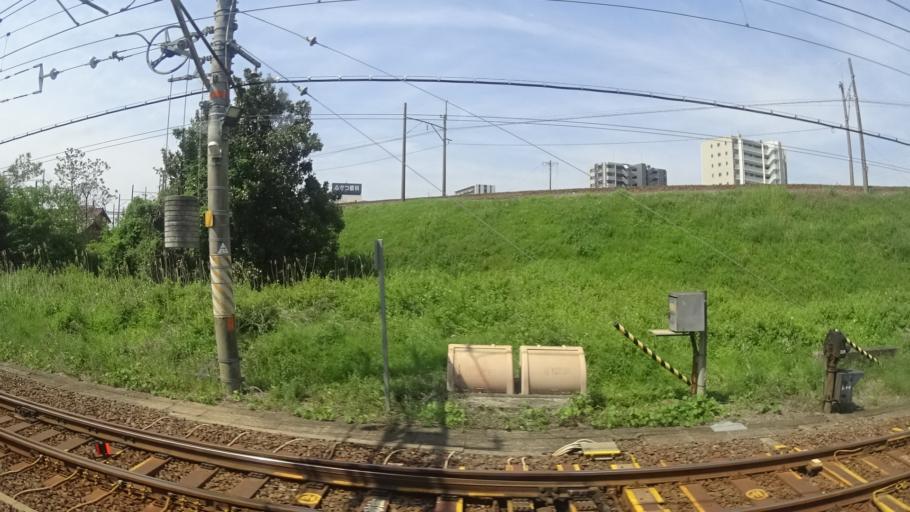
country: JP
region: Mie
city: Yokkaichi
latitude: 35.0110
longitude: 136.6516
